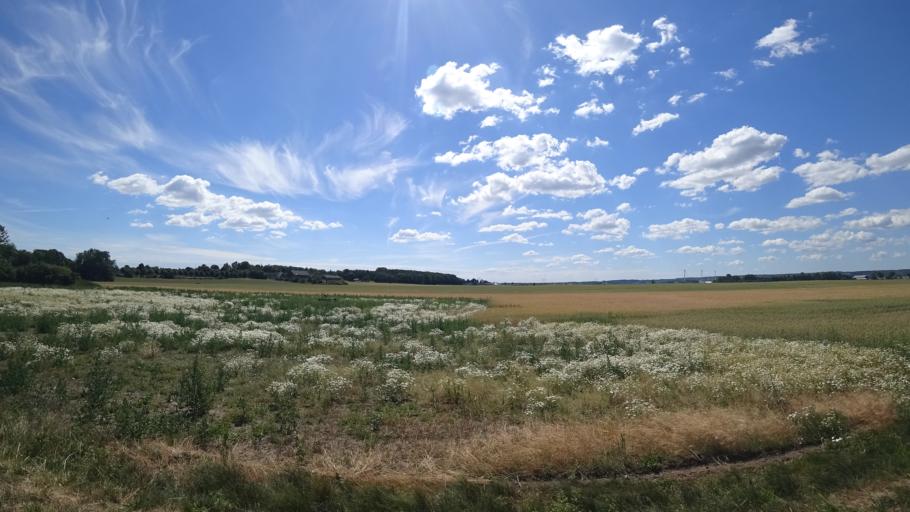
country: SE
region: Skane
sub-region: Kristianstads Kommun
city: Onnestad
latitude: 56.0730
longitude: 14.0769
